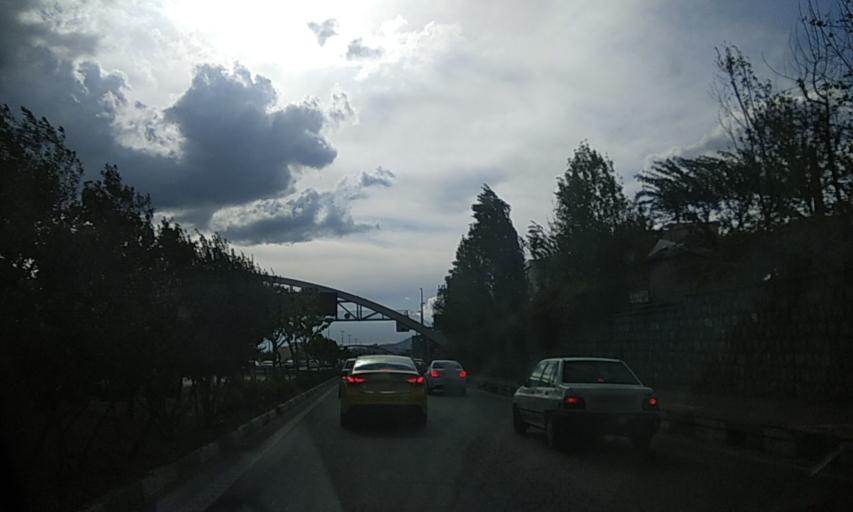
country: IR
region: Tehran
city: Tehran
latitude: 35.7536
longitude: 51.2911
